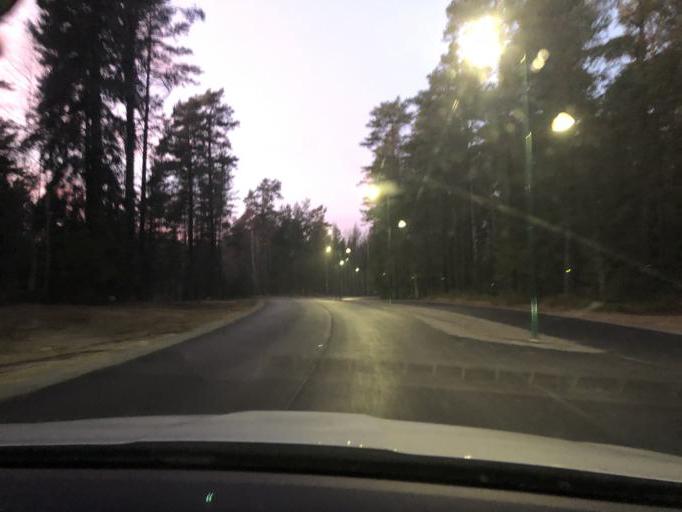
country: SE
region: Stockholm
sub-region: Botkyrka Kommun
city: Varsta
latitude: 59.1728
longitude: 17.7990
